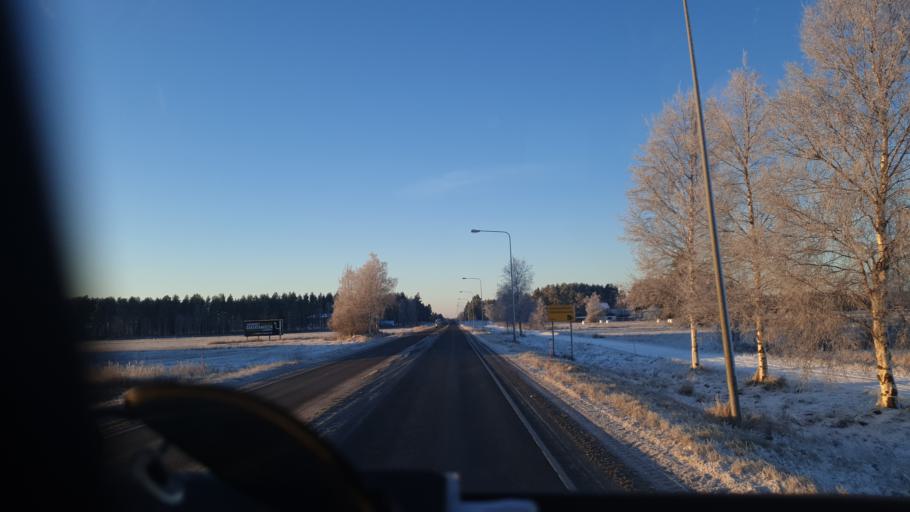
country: FI
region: Northern Ostrobothnia
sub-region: Ylivieska
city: Kalajoki
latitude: 64.2511
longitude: 23.9096
